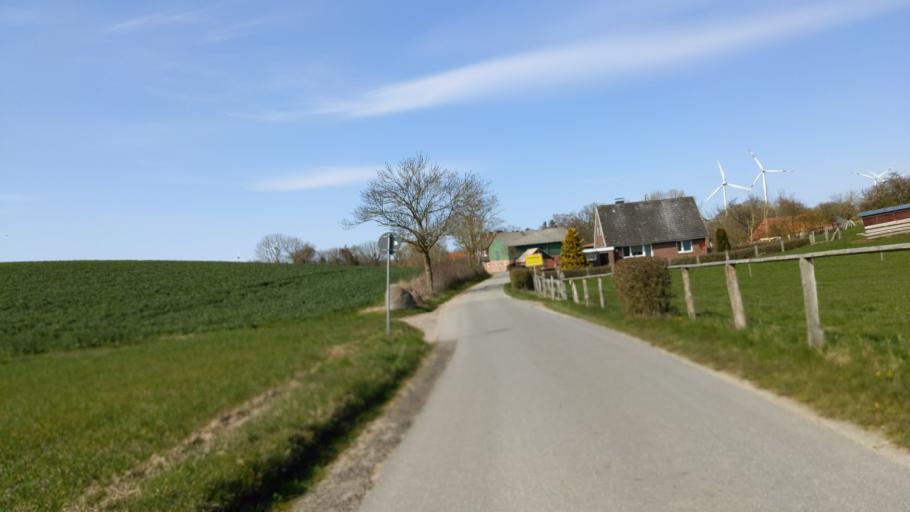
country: DE
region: Schleswig-Holstein
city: Schashagen
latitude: 54.1318
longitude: 10.8848
